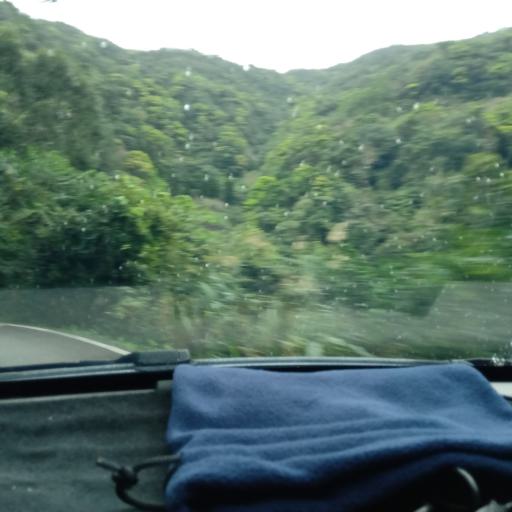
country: TW
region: Taiwan
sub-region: Yilan
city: Yilan
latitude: 24.8119
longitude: 121.7017
